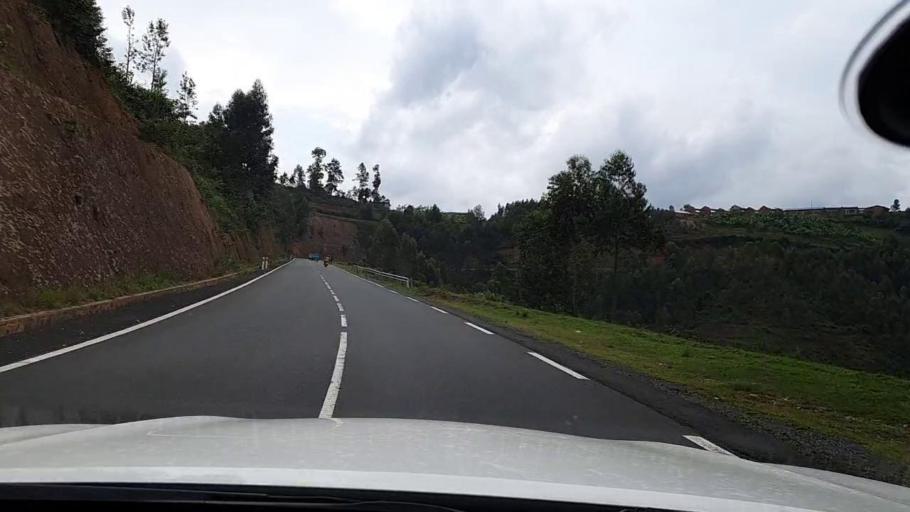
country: RW
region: Western Province
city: Kibuye
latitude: -2.1726
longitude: 29.2906
